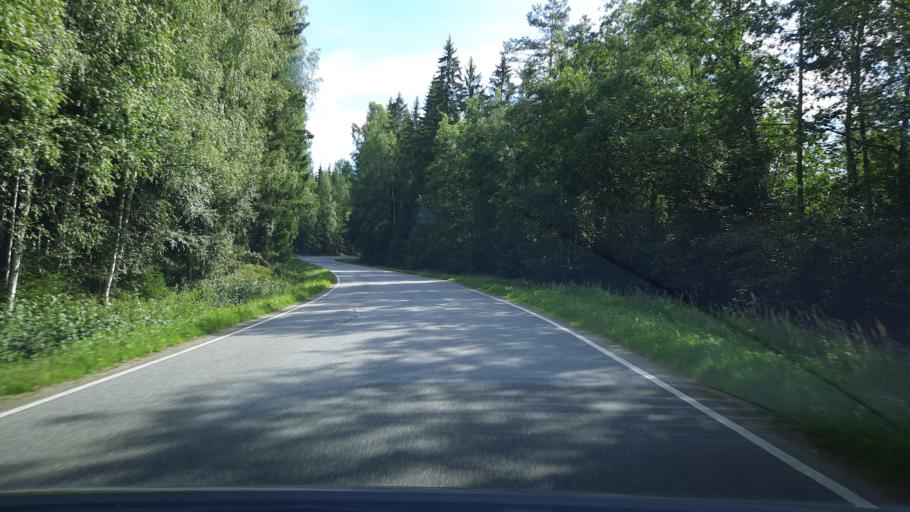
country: FI
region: Pirkanmaa
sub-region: Etelae-Pirkanmaa
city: Urjala
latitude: 61.1769
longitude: 23.3629
